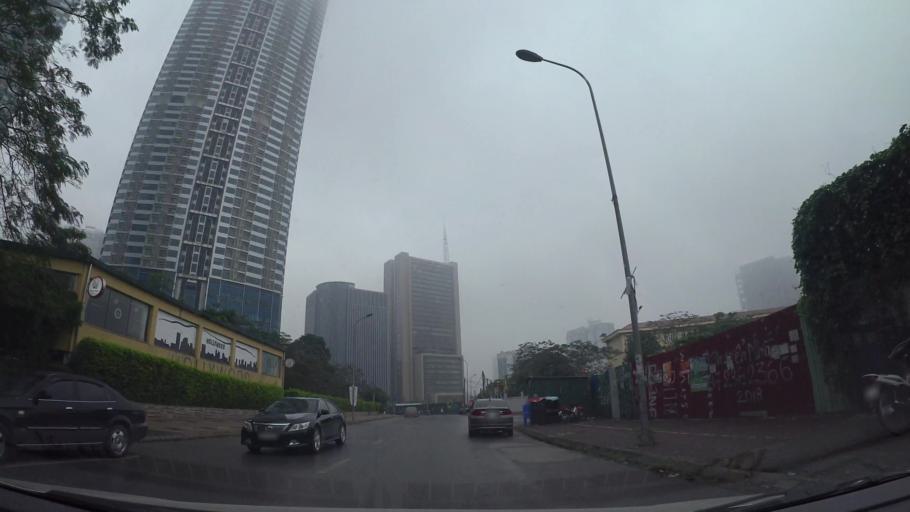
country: VN
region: Ha Noi
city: Cau Giay
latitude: 21.0172
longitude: 105.7851
